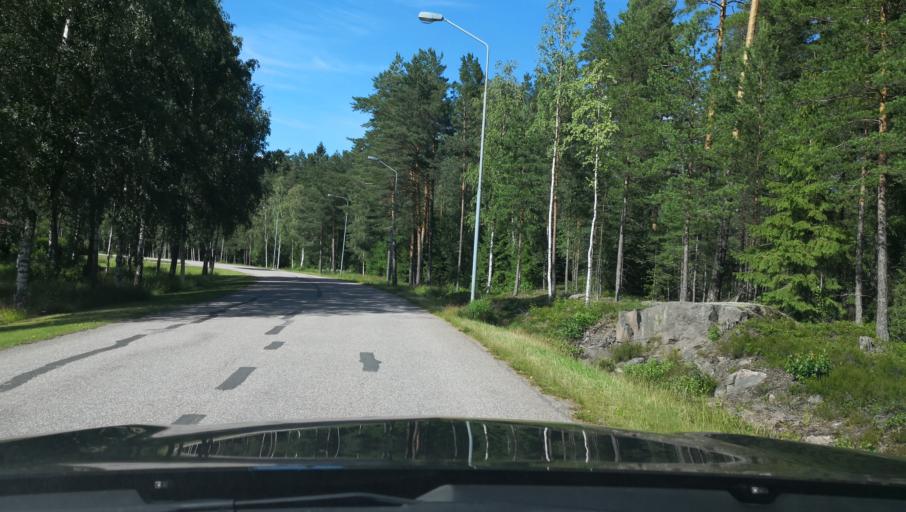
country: SE
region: Vaestmanland
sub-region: Surahammars Kommun
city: Surahammar
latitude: 59.6930
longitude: 16.2444
